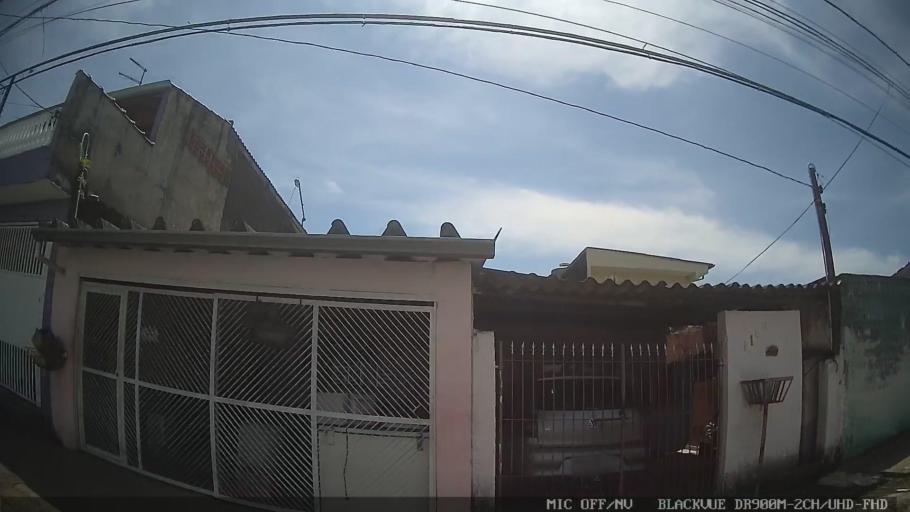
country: BR
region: Sao Paulo
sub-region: Suzano
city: Suzano
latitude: -23.5216
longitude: -46.3063
